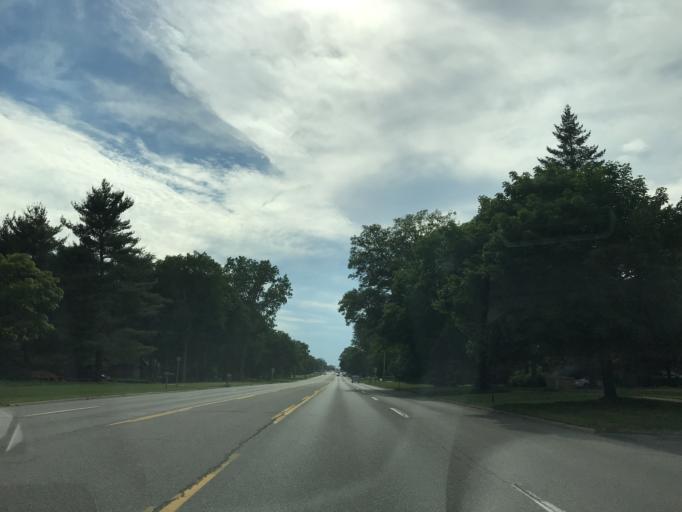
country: US
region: Michigan
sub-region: Wayne County
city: Livonia
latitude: 42.4120
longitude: -83.3662
